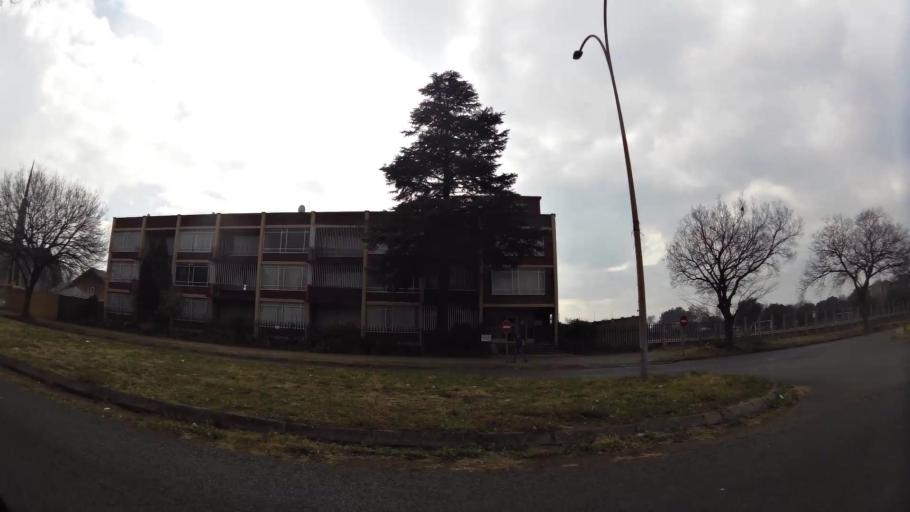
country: ZA
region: Gauteng
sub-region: Sedibeng District Municipality
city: Vanderbijlpark
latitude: -26.6930
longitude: 27.8311
